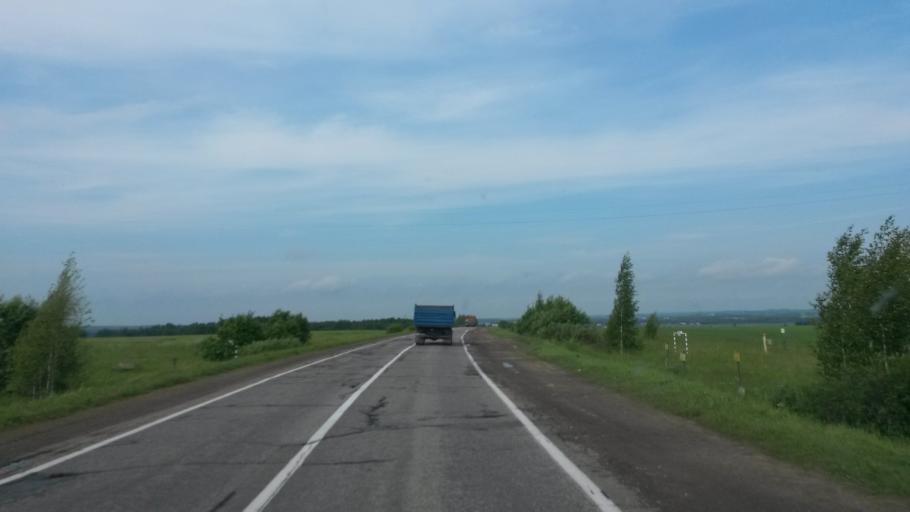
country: RU
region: Jaroslavl
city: Gavrilov-Yam
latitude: 57.3085
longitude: 39.9241
